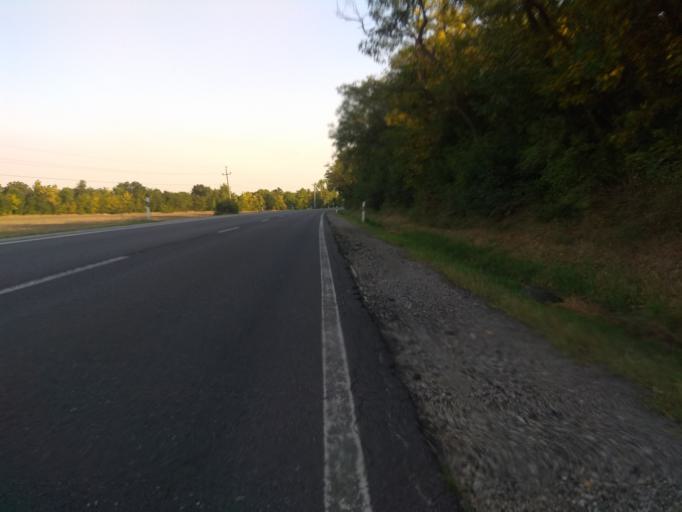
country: HU
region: Borsod-Abauj-Zemplen
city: Nyekladhaza
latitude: 47.9635
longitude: 20.8337
